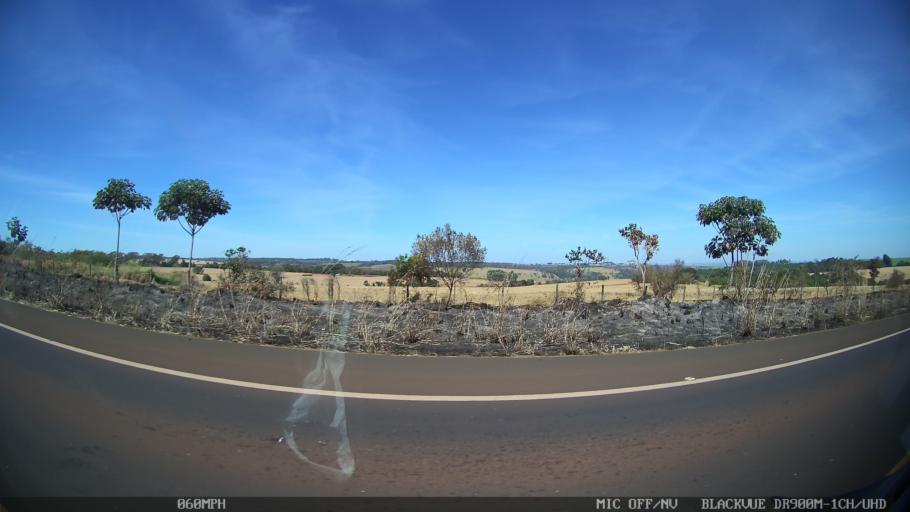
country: BR
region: Sao Paulo
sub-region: Franca
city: Franca
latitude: -20.5512
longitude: -47.4868
